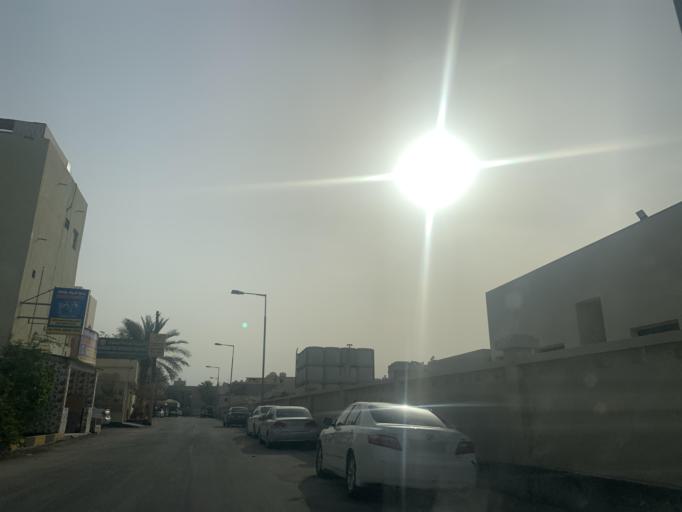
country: BH
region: Northern
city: Ar Rifa'
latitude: 26.1344
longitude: 50.5589
